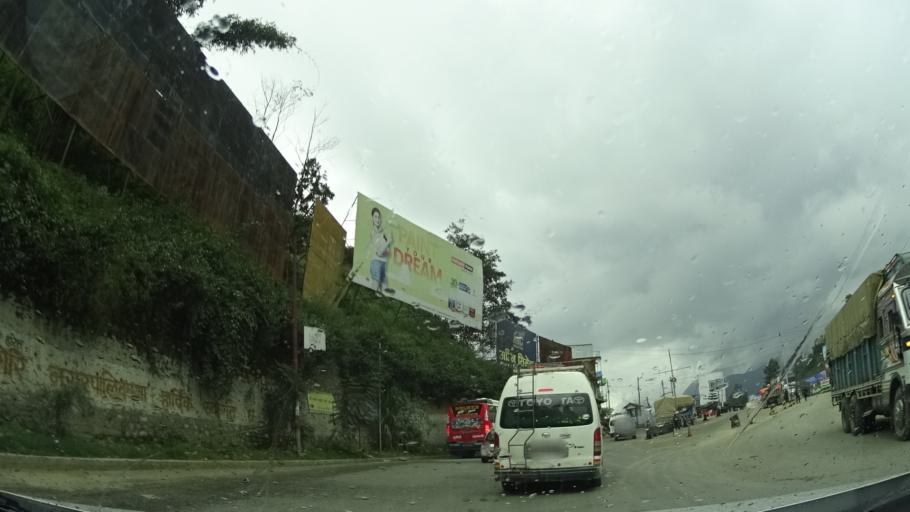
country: NP
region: Central Region
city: Kirtipur
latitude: 27.7073
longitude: 85.2053
